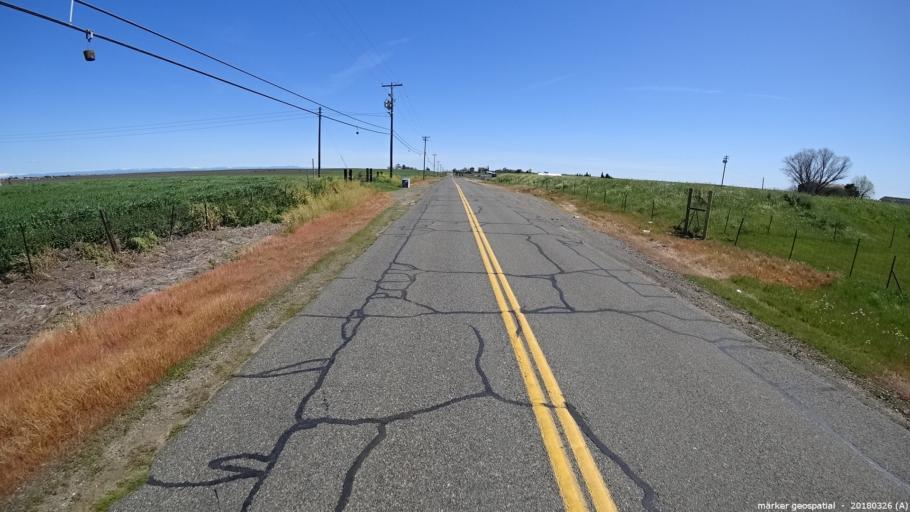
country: US
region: California
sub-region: Sacramento County
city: Wilton
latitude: 38.4713
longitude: -121.2549
